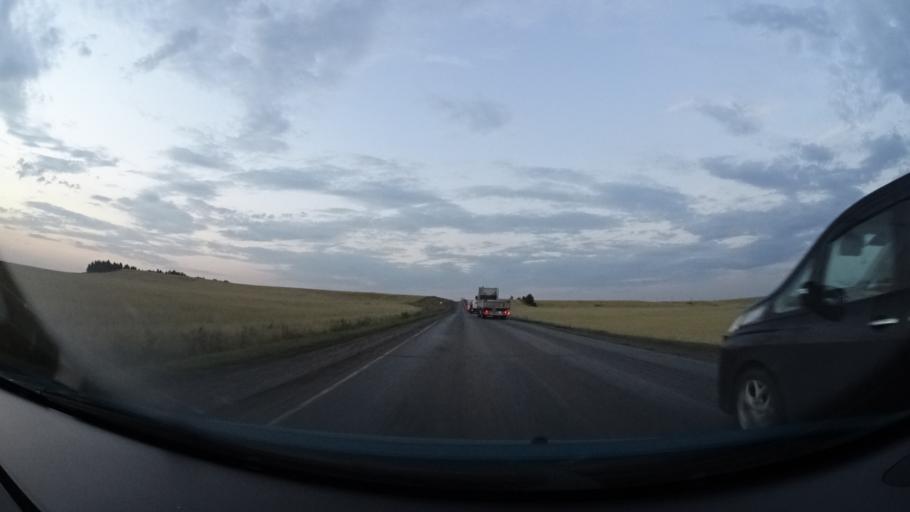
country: RU
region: Tatarstan
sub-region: Bavlinskiy Rayon
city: Bavly
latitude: 54.2921
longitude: 53.0027
